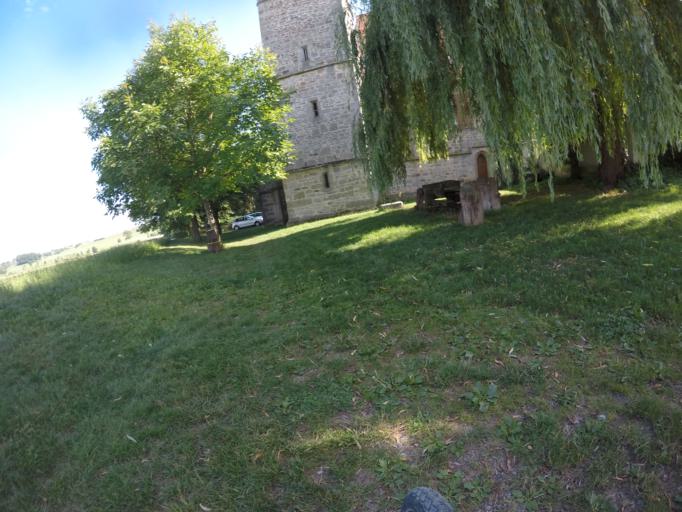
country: DE
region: Baden-Wuerttemberg
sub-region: Regierungsbezirk Stuttgart
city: Altdorf
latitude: 48.6514
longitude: 8.9794
